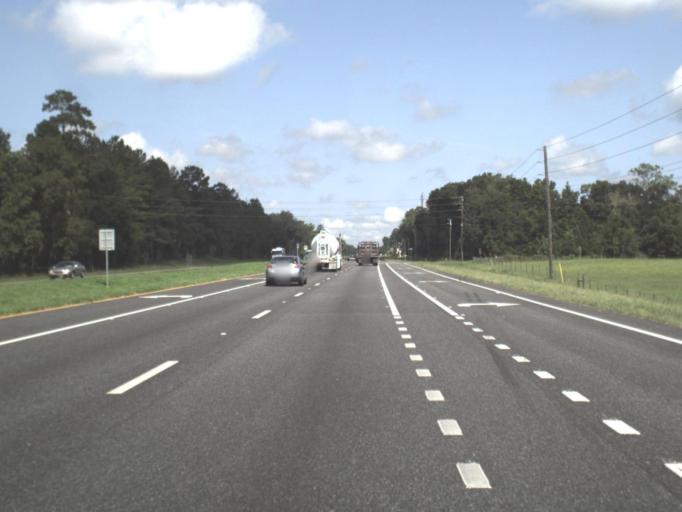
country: US
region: Florida
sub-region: Hernando County
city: Hill 'n Dale
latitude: 28.5265
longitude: -82.3157
